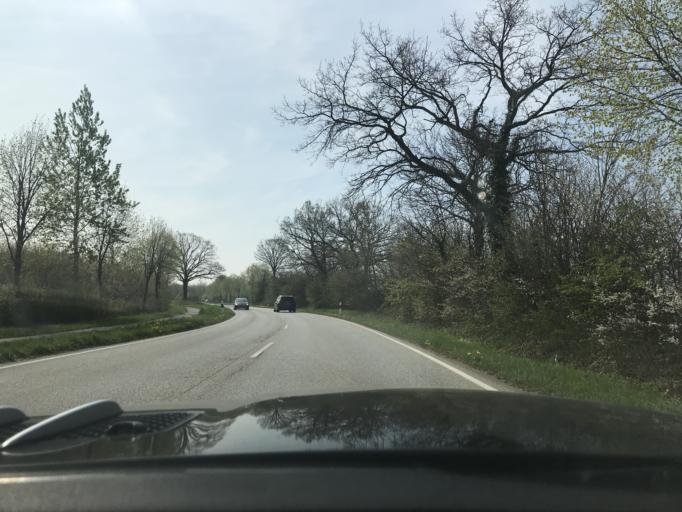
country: DE
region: Schleswig-Holstein
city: Gromitz
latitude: 54.1752
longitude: 10.9766
